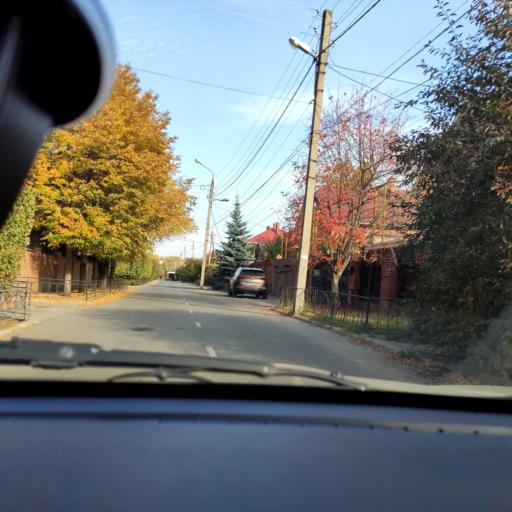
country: RU
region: Samara
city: Tol'yatti
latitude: 53.5343
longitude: 49.3883
